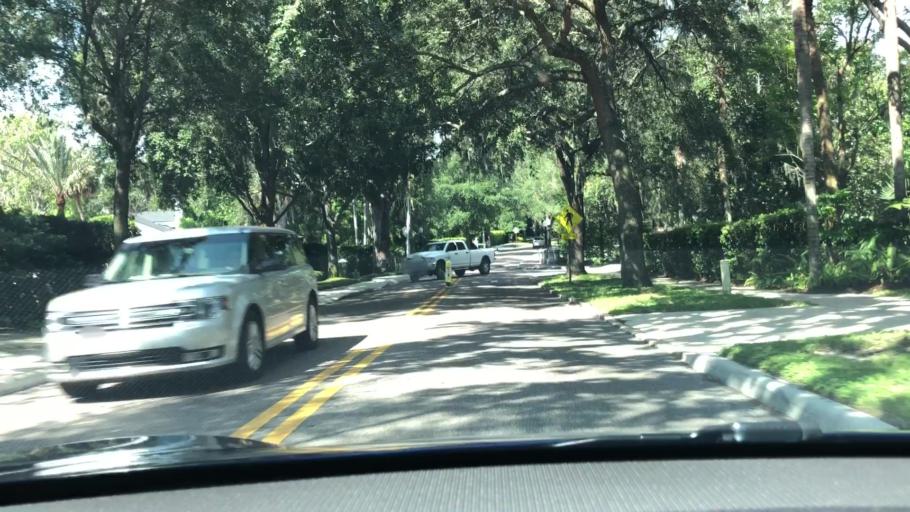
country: US
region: Florida
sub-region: Orange County
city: Winter Park
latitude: 28.6082
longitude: -81.3426
